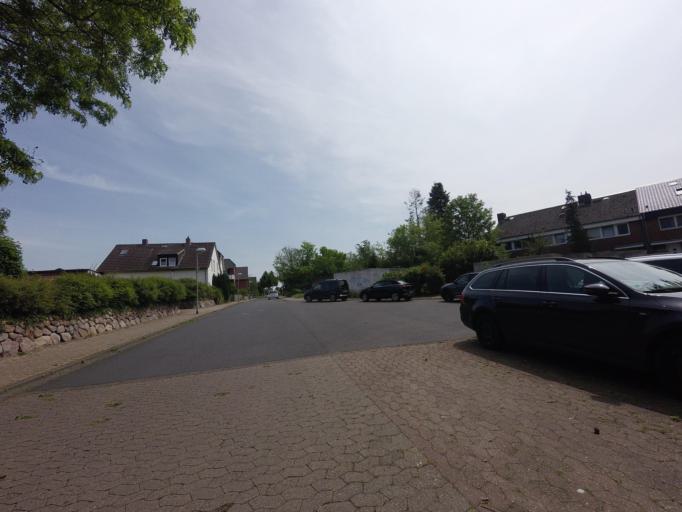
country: DE
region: Lower Saxony
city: Braunschweig
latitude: 52.3086
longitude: 10.4846
